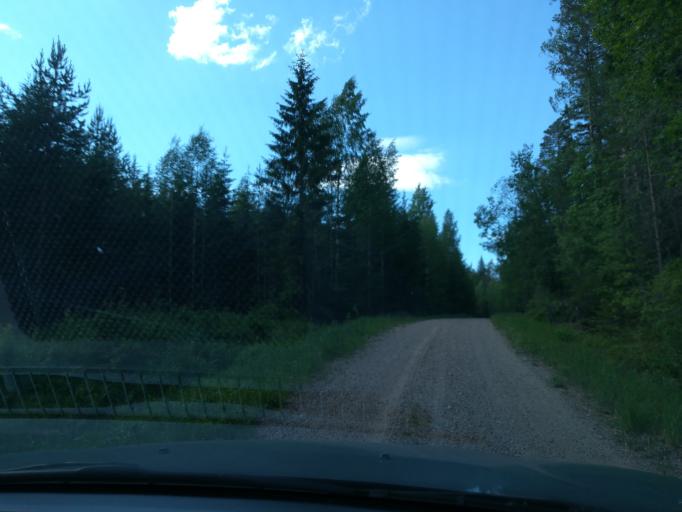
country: FI
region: South Karelia
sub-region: Imatra
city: Ruokolahti
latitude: 61.5413
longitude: 28.8110
